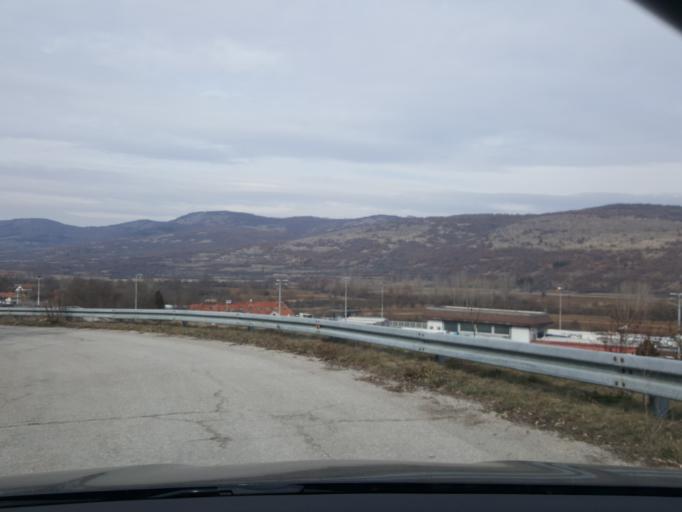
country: RS
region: Central Serbia
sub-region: Pirotski Okrug
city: Dimitrovgrad
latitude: 42.9989
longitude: 22.8248
